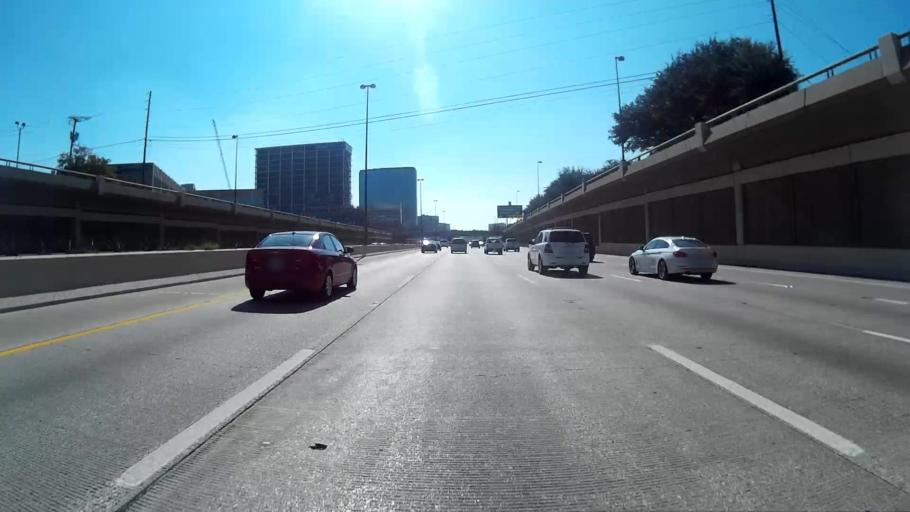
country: US
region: Texas
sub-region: Dallas County
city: Highland Park
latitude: 32.8445
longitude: -96.7743
